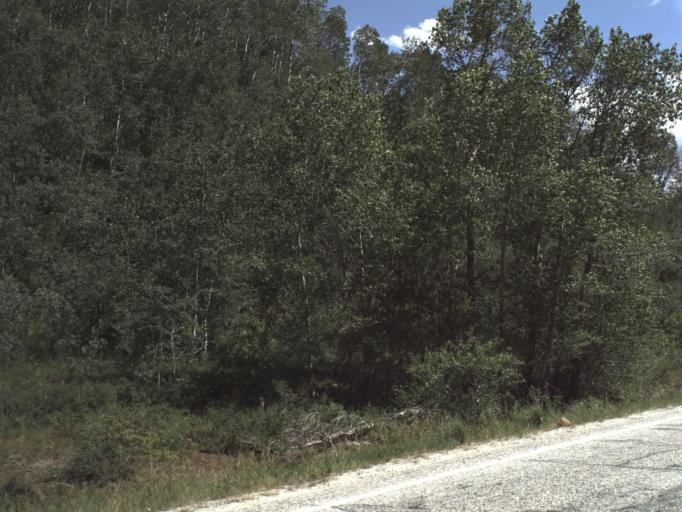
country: US
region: Utah
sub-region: Weber County
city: Wolf Creek
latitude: 41.3999
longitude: -111.5995
